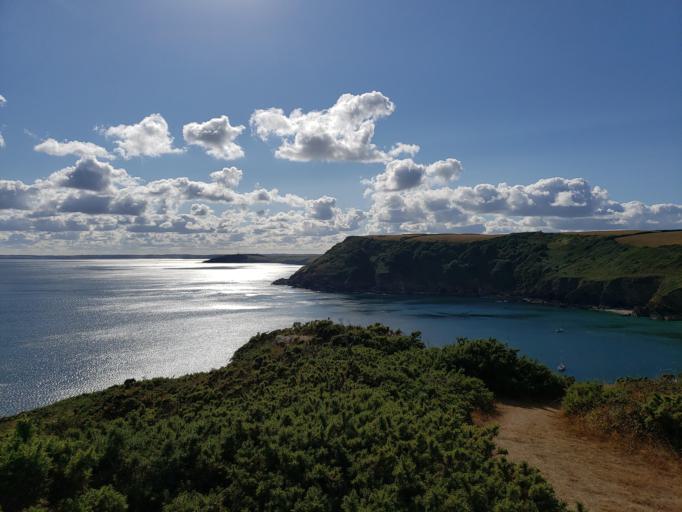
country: GB
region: England
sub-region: Cornwall
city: Fowey
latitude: 50.3252
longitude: -4.6003
